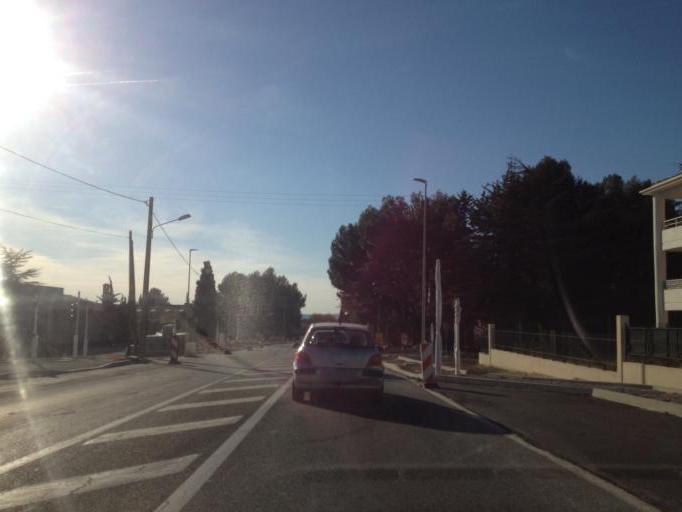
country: FR
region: Provence-Alpes-Cote d'Azur
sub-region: Departement des Bouches-du-Rhone
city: Saint-Cannat
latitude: 43.6182
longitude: 5.3082
